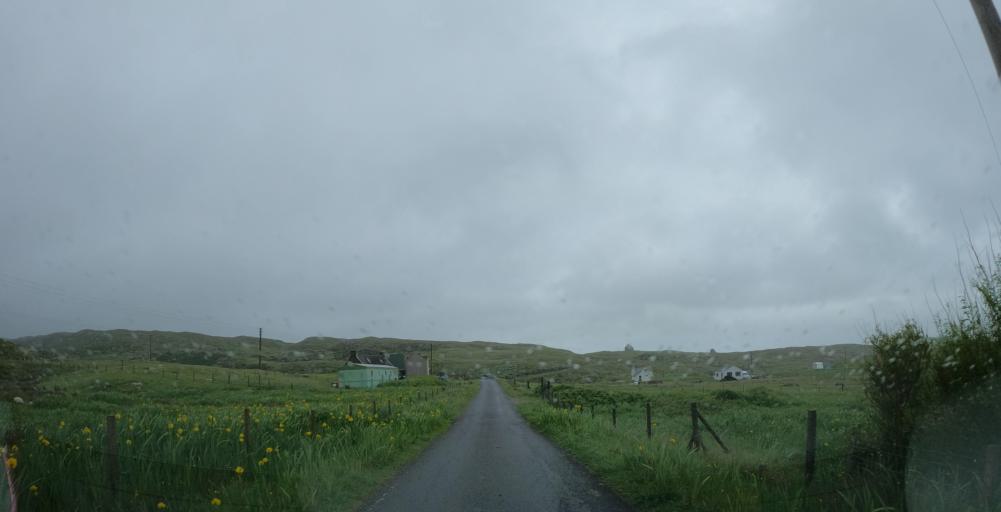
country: GB
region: Scotland
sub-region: Eilean Siar
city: Barra
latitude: 56.9740
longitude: -7.4228
